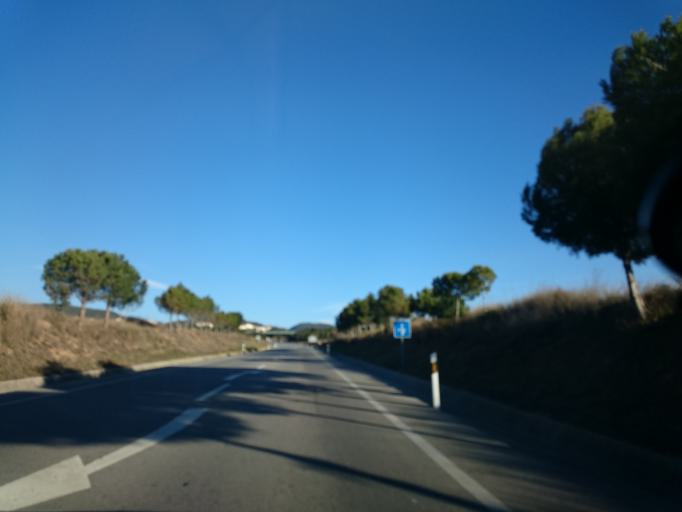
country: ES
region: Catalonia
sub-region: Provincia de Barcelona
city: Sant Pere de Ribes
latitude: 41.2568
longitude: 1.7830
